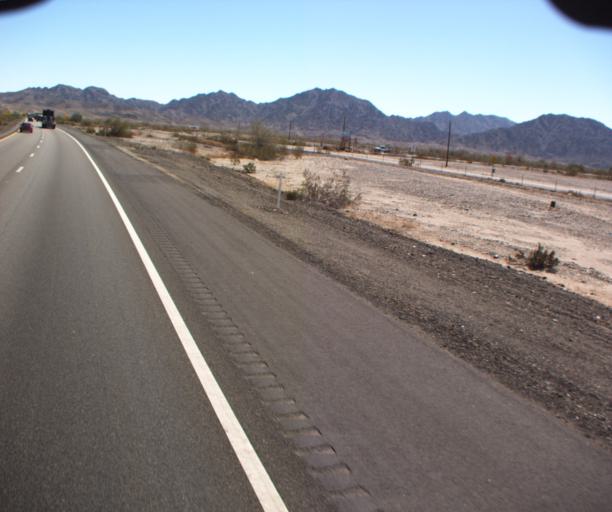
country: US
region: Arizona
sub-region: Yuma County
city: Fortuna Foothills
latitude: 32.6611
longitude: -114.3770
